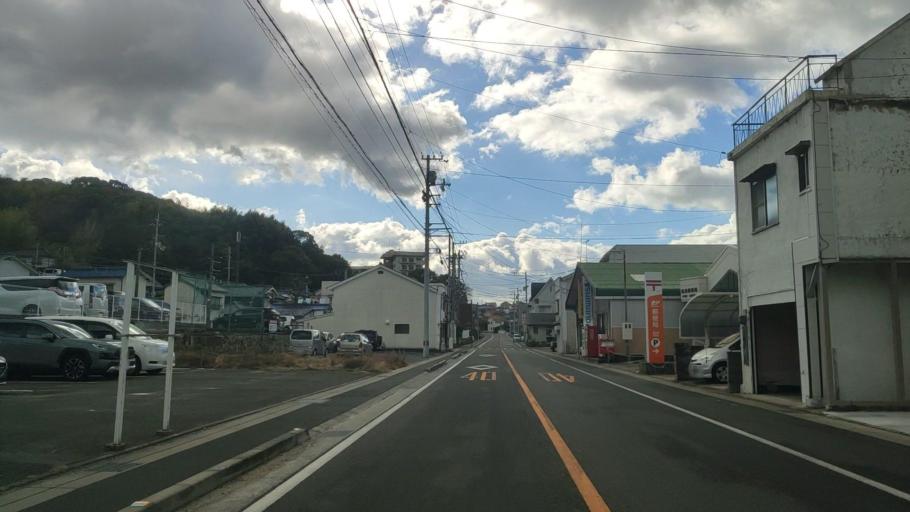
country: JP
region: Ehime
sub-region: Shikoku-chuo Shi
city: Matsuyama
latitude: 33.8832
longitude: 132.7018
